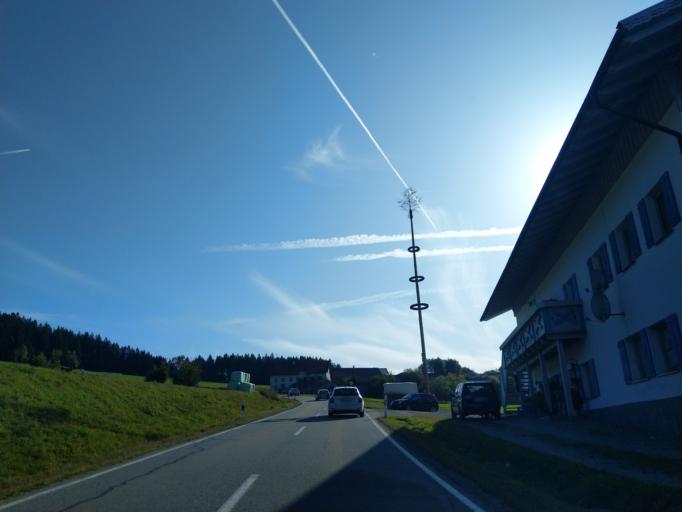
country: DE
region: Bavaria
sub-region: Lower Bavaria
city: Achslach
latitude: 48.9455
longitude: 12.9250
